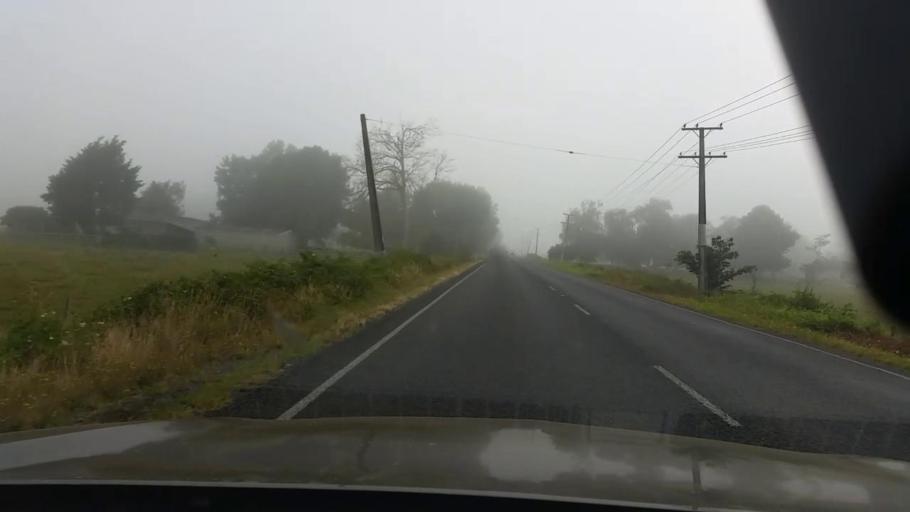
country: NZ
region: Waikato
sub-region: Hamilton City
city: Hamilton
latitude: -37.6326
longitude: 175.3081
